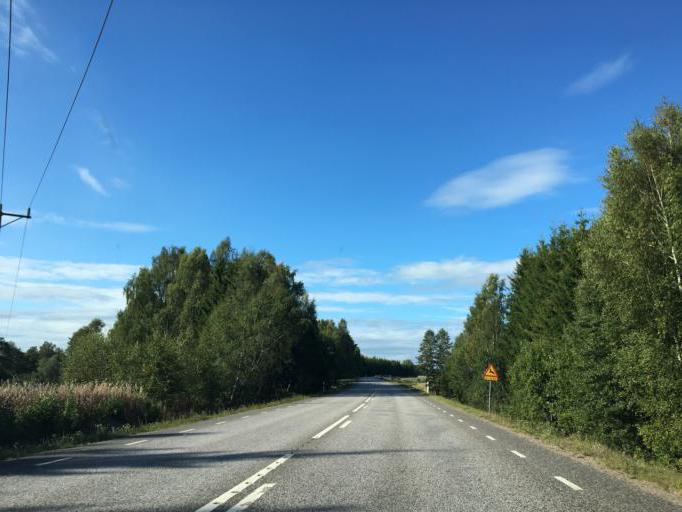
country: SE
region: Soedermanland
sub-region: Nykopings Kommun
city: Nykoping
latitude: 58.8288
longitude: 16.9274
